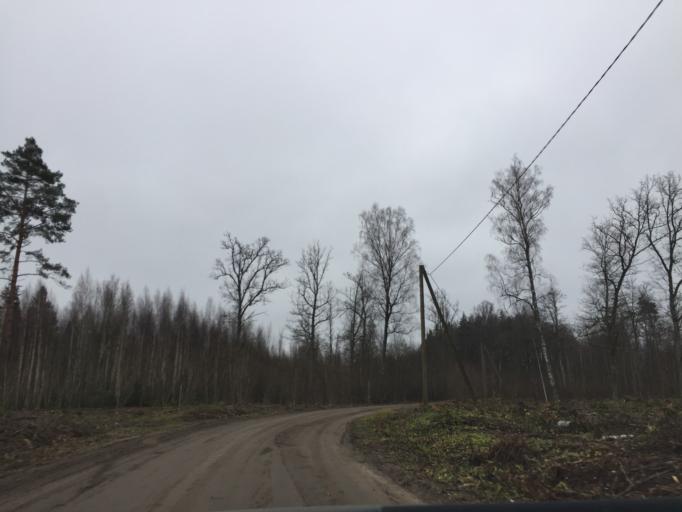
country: LV
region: Limbazu Rajons
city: Limbazi
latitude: 57.4989
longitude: 24.7703
